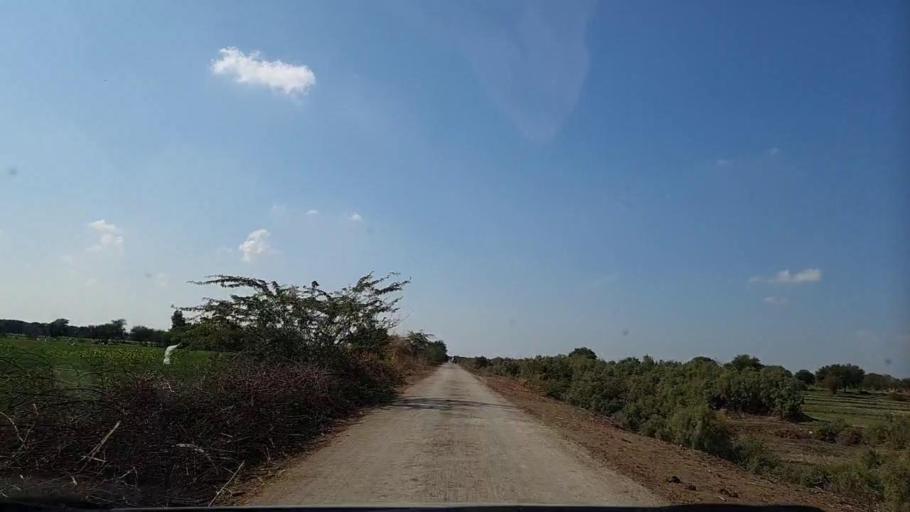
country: PK
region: Sindh
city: Pithoro
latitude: 25.6689
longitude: 69.4673
